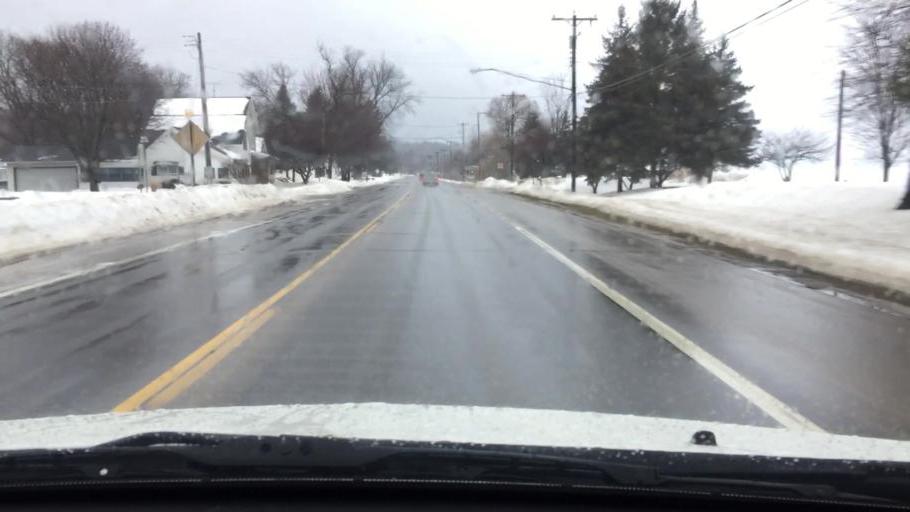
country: US
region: Michigan
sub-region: Charlevoix County
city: East Jordan
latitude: 45.1559
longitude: -85.1418
